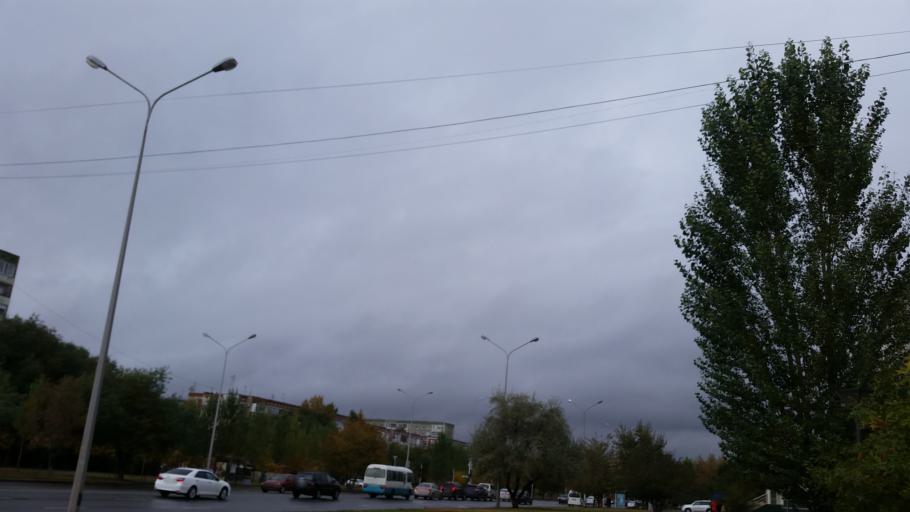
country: KZ
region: Astana Qalasy
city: Astana
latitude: 51.1510
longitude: 71.4820
